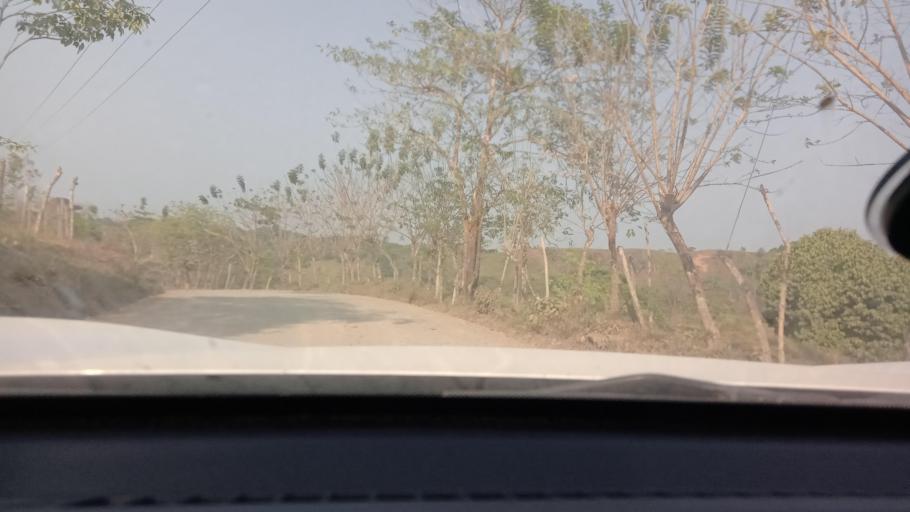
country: MX
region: Tabasco
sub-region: Huimanguillo
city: Francisco Rueda
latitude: 17.6581
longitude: -93.8639
